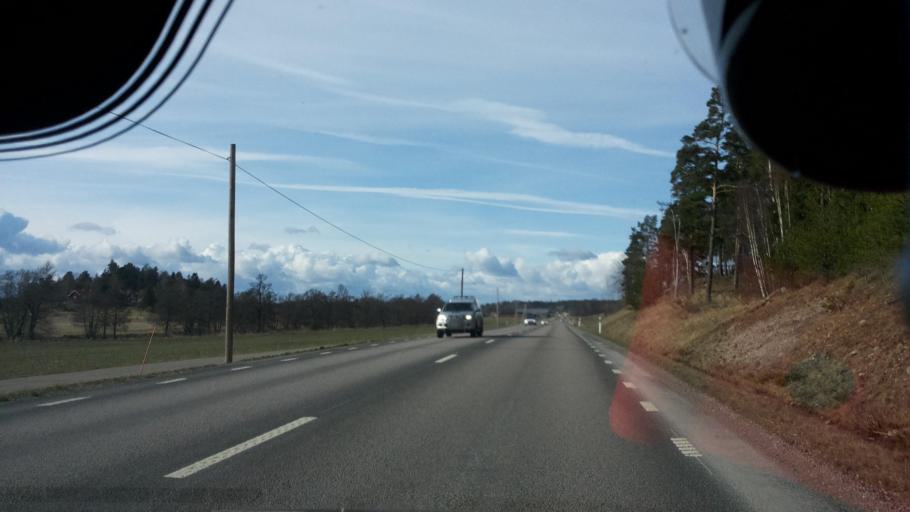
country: SE
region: Soedermanland
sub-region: Trosa Kommun
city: Trosa
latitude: 58.9175
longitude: 17.5443
